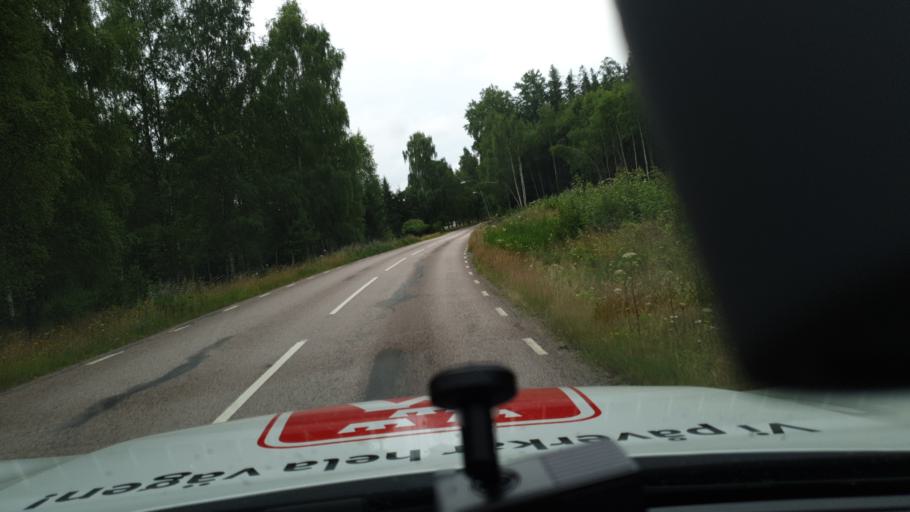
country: SE
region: Vaermland
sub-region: Sunne Kommun
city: Sunne
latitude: 59.7775
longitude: 13.2354
